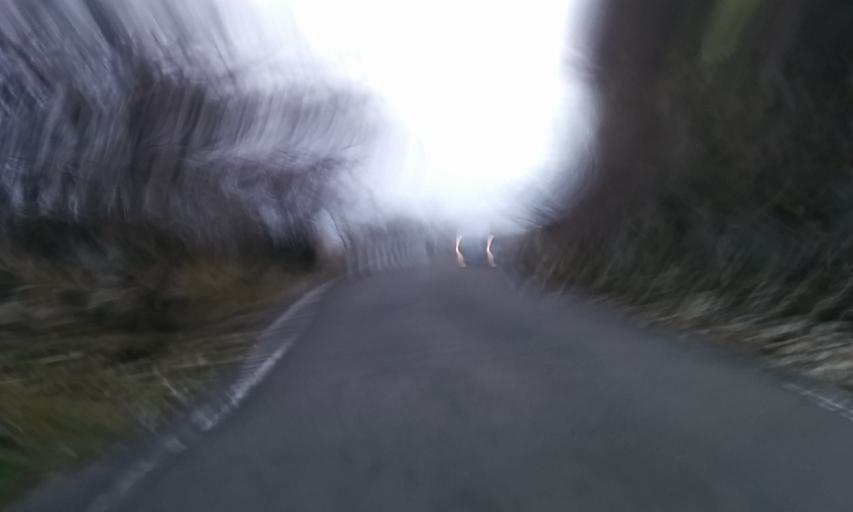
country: JP
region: Ehime
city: Saijo
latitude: 33.7821
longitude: 133.2333
